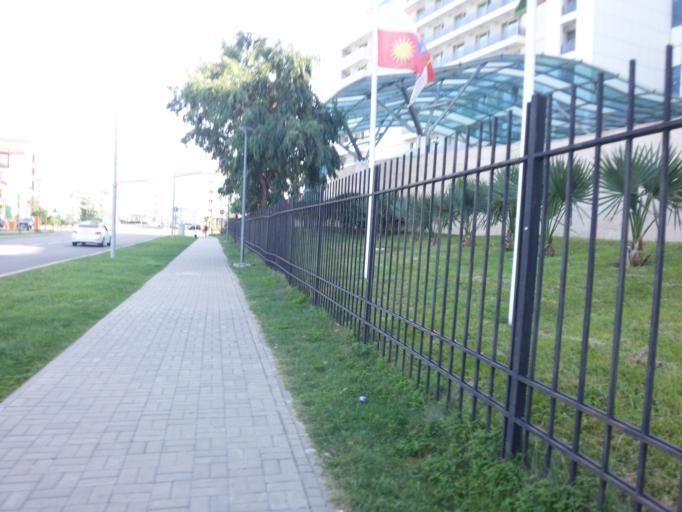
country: RU
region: Krasnodarskiy
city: Adler
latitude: 43.4101
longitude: 39.9386
